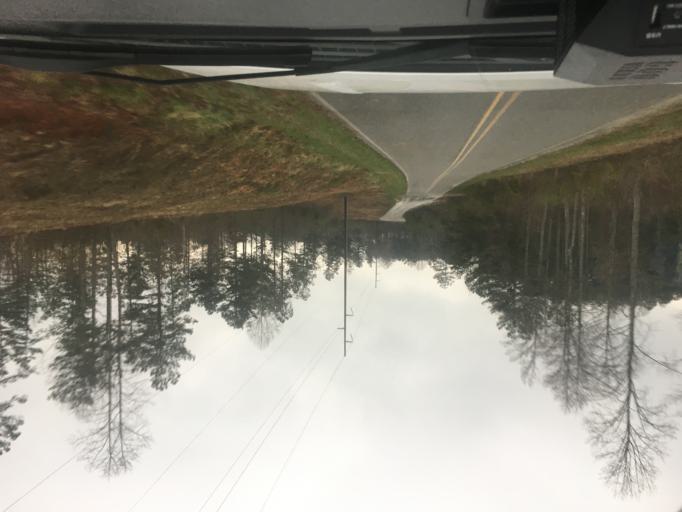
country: US
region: Georgia
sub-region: Dawson County
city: Dawsonville
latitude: 34.4405
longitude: -84.2234
